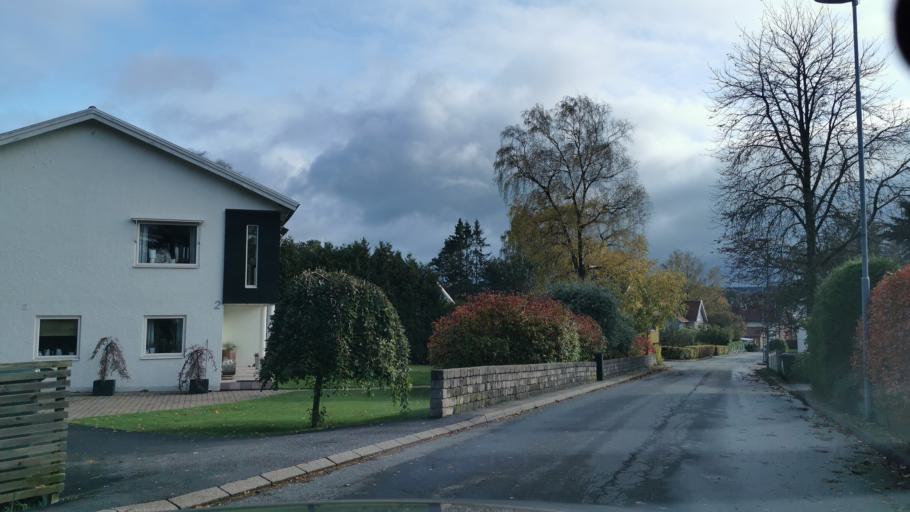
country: SE
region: Vaestra Goetaland
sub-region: Partille Kommun
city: Partille
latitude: 57.7273
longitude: 12.0758
